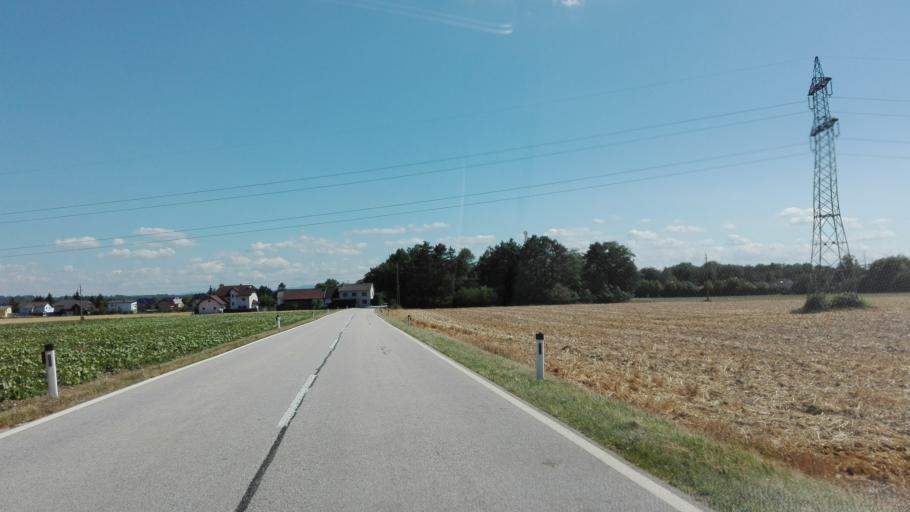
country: AT
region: Upper Austria
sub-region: Wels-Land
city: Marchtrenk
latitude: 48.2049
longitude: 14.1347
